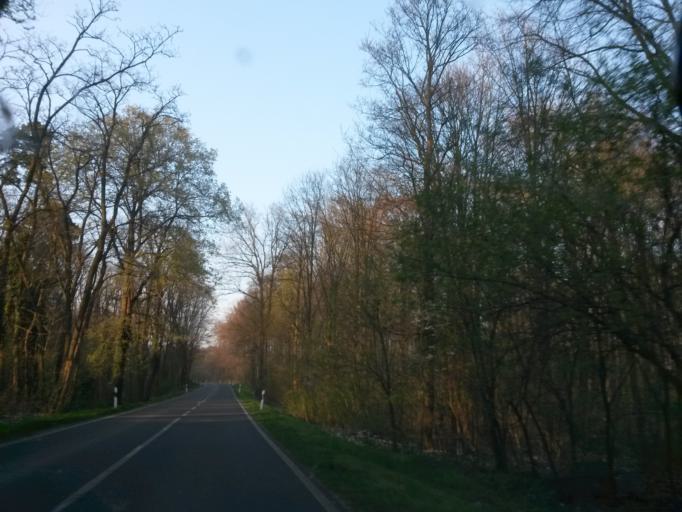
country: DE
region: Brandenburg
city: Rehfelde
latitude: 52.5406
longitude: 13.9364
